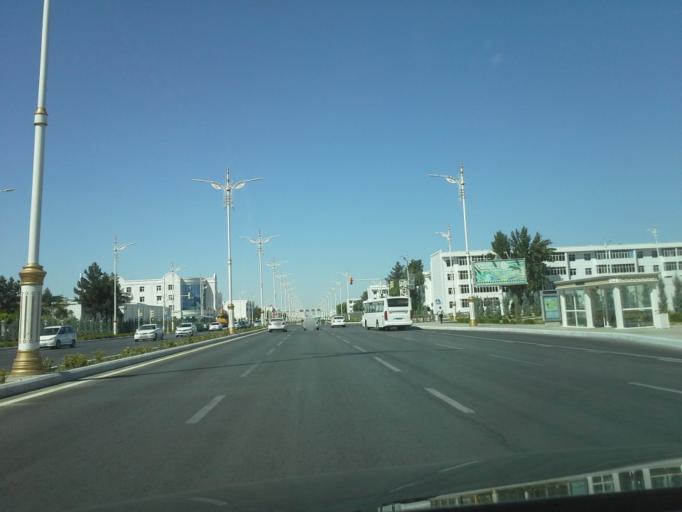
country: TM
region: Ahal
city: Ashgabat
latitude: 37.9572
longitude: 58.3763
